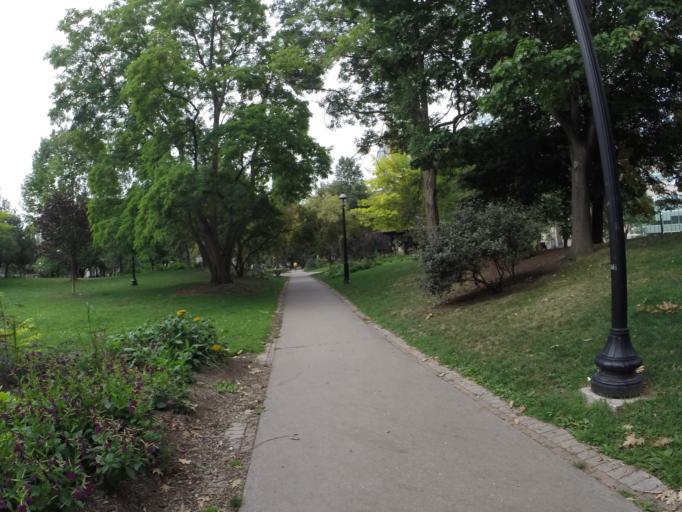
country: CA
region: Ontario
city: Toronto
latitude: 43.6522
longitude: -79.3726
